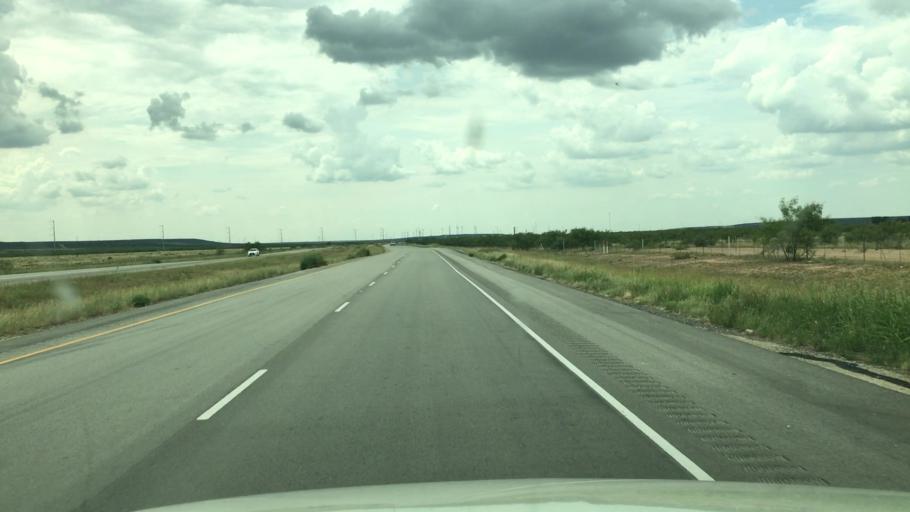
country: US
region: Texas
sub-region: Sterling County
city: Sterling City
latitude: 31.9615
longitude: -101.2148
